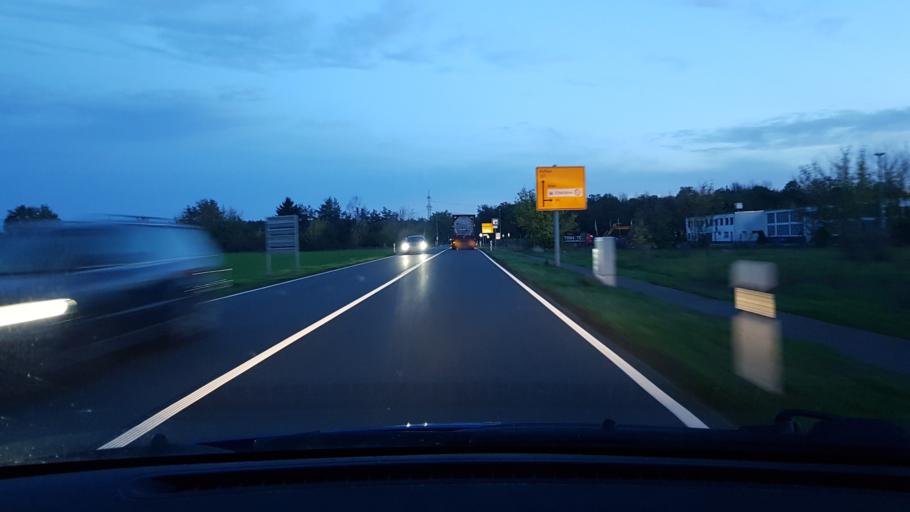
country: DE
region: Saxony-Anhalt
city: Zerbst
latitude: 51.9512
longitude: 12.1070
